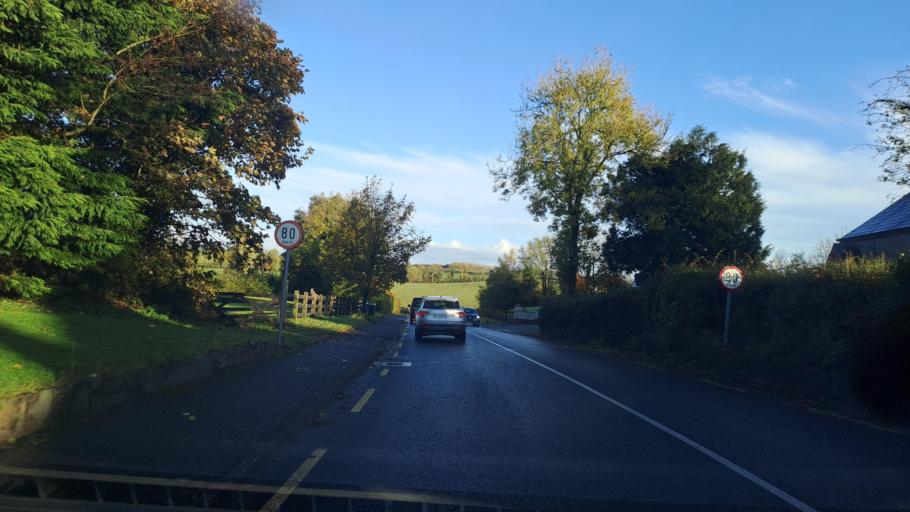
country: IE
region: Ulster
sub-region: An Cabhan
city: Cootehill
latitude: 54.1211
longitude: -7.0085
